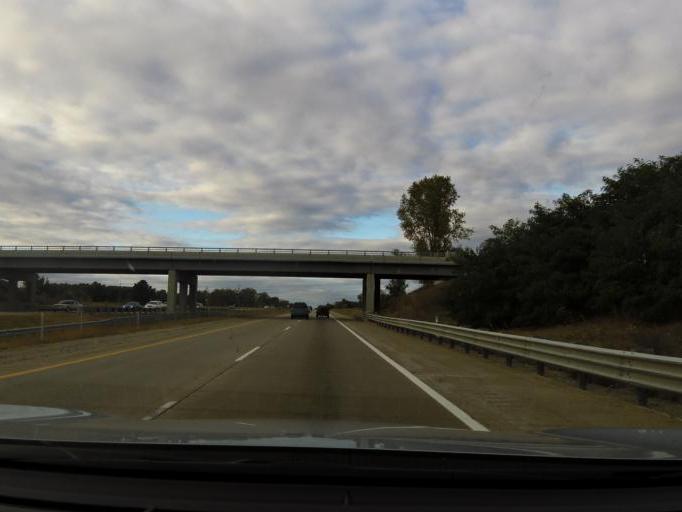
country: US
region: Michigan
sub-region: Genesee County
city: Fenton
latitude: 42.6762
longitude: -83.7597
